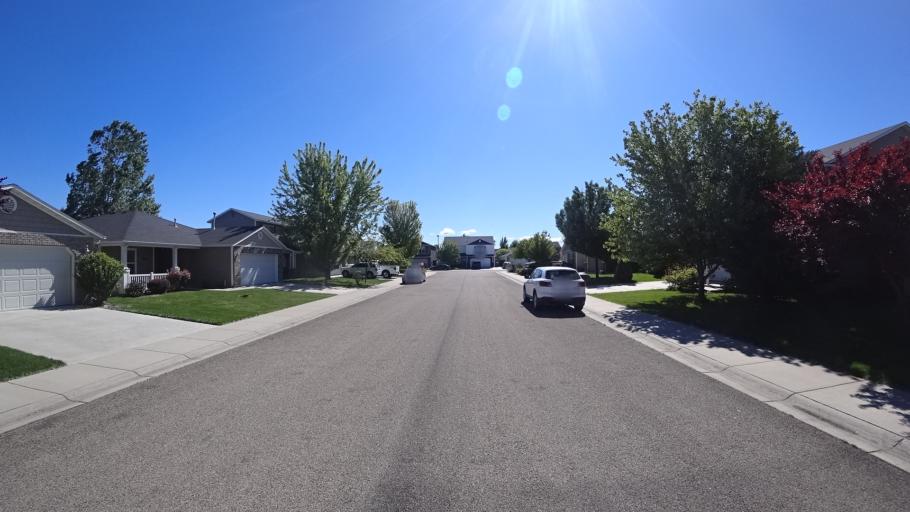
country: US
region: Idaho
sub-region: Ada County
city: Meridian
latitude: 43.6450
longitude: -116.3906
